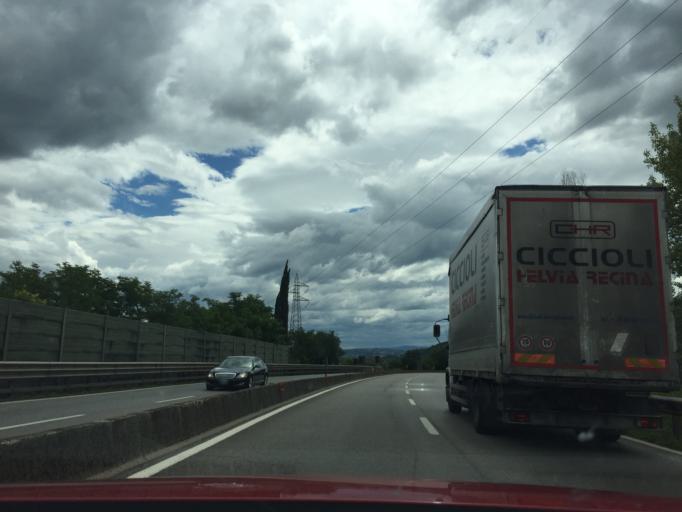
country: IT
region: Tuscany
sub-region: Province of Florence
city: Montelupo Fiorentino
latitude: 43.7247
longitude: 11.0204
